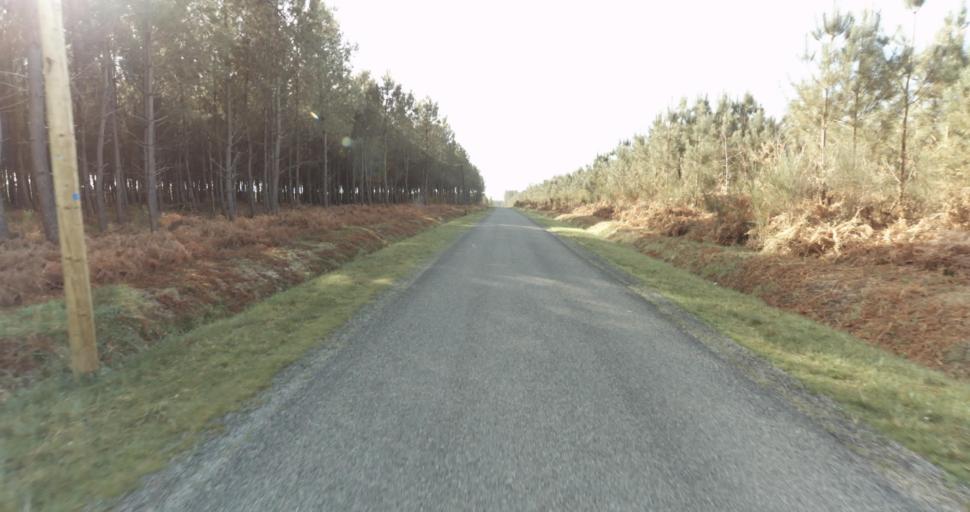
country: FR
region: Aquitaine
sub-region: Departement des Landes
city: Sarbazan
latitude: 44.0172
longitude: -0.2355
